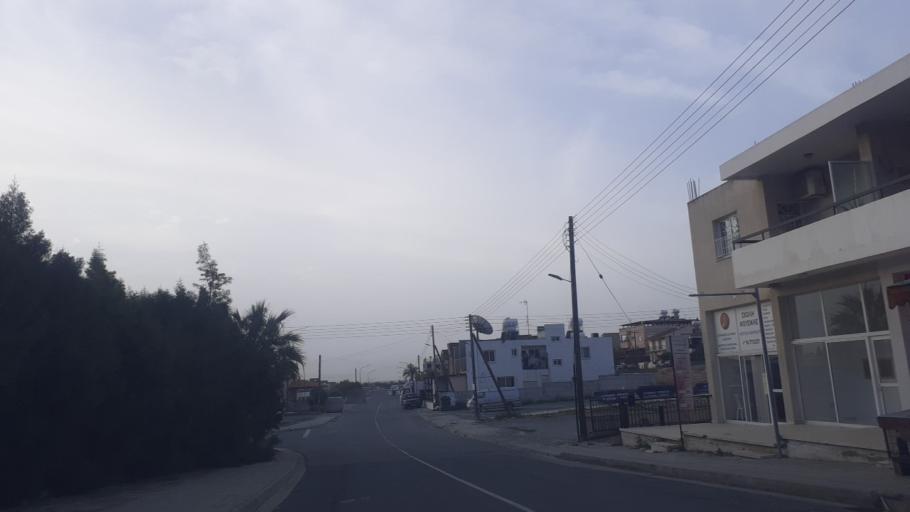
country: CY
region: Larnaka
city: Kolossi
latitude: 34.6573
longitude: 32.9566
